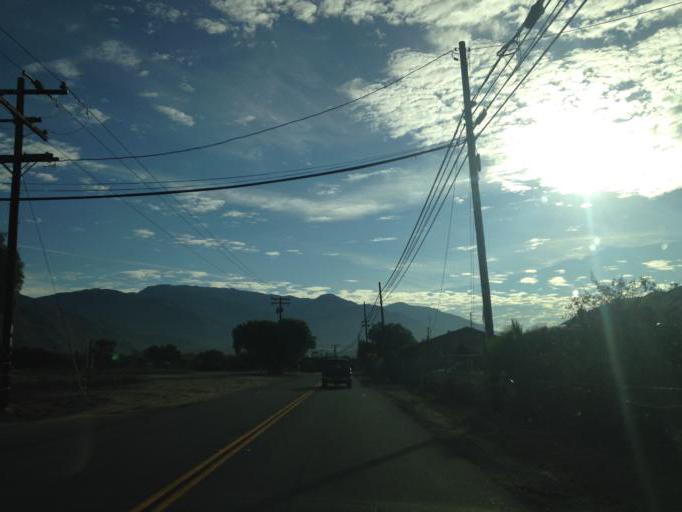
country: US
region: California
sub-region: San Diego County
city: Rainbow
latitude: 33.3647
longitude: -117.0690
